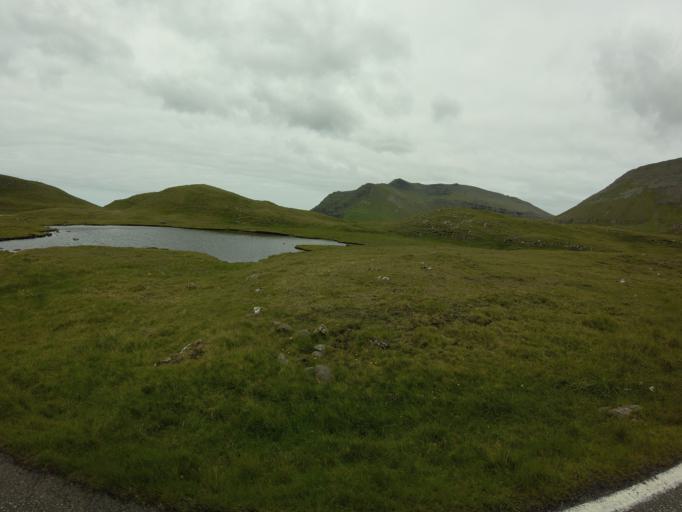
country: FO
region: Suduroy
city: Tvoroyri
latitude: 61.5167
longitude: -6.8682
